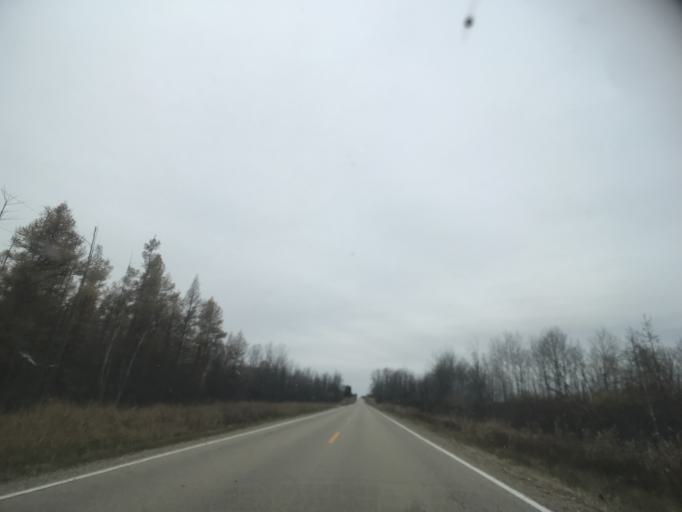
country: US
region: Wisconsin
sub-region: Oconto County
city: Gillett
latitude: 44.9835
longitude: -88.3045
